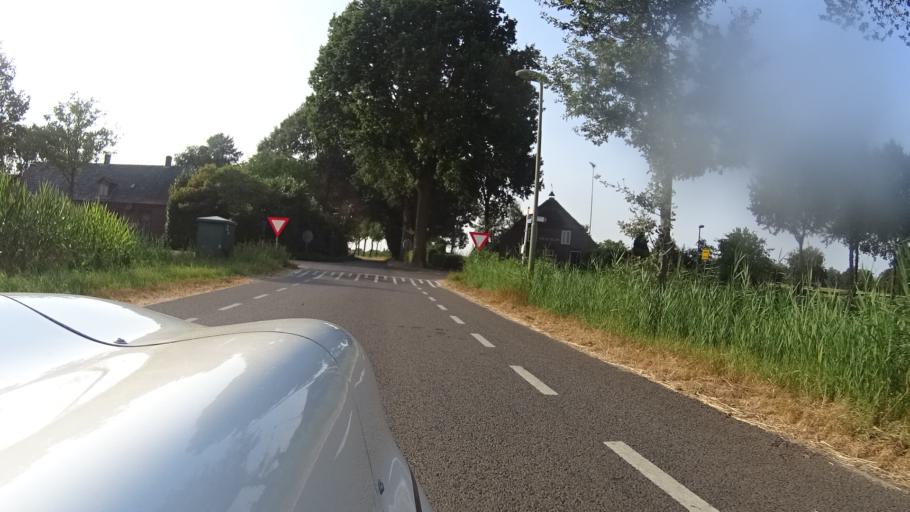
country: NL
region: North Brabant
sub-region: Gemeente Landerd
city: Zeeland
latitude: 51.6919
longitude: 5.7143
